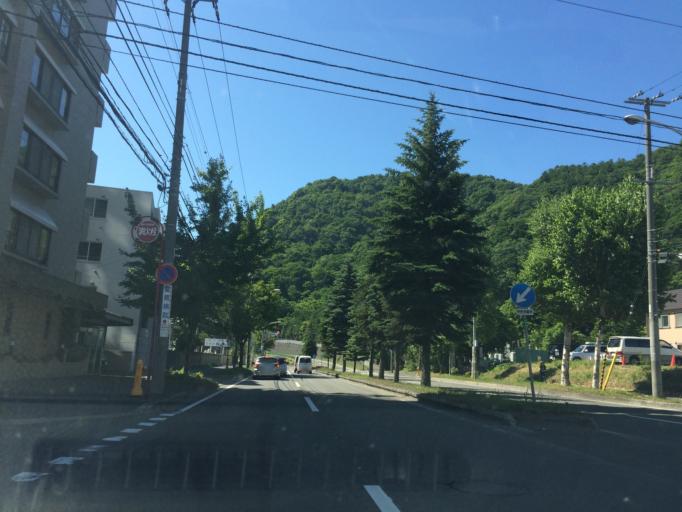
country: JP
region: Hokkaido
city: Sapporo
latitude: 43.0532
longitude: 141.3163
